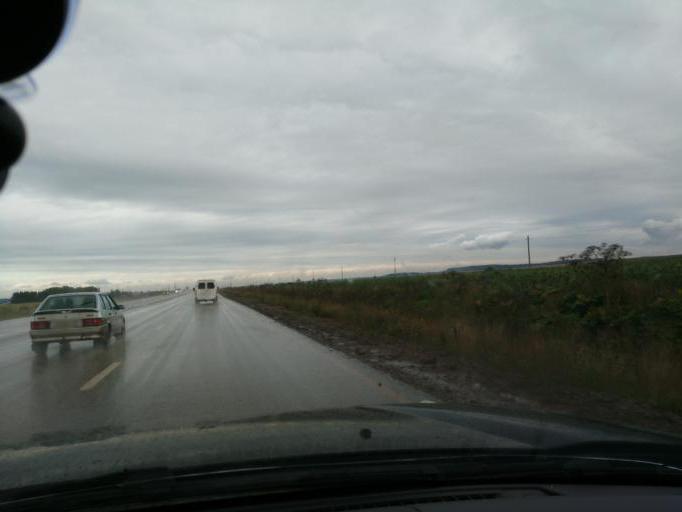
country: RU
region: Perm
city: Kultayevo
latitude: 57.8787
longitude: 55.9105
